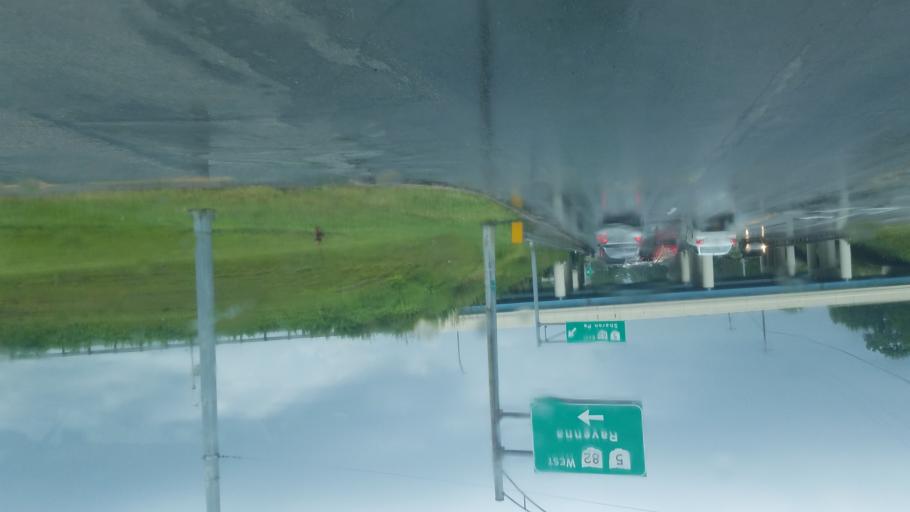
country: US
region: Ohio
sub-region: Trumbull County
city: Champion Heights
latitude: 41.2766
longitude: -80.8421
